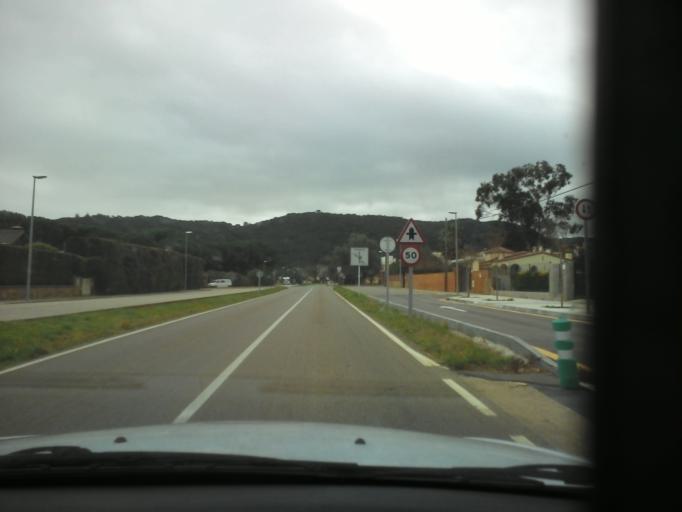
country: ES
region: Catalonia
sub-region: Provincia de Girona
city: Calonge
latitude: 41.8554
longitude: 3.0622
